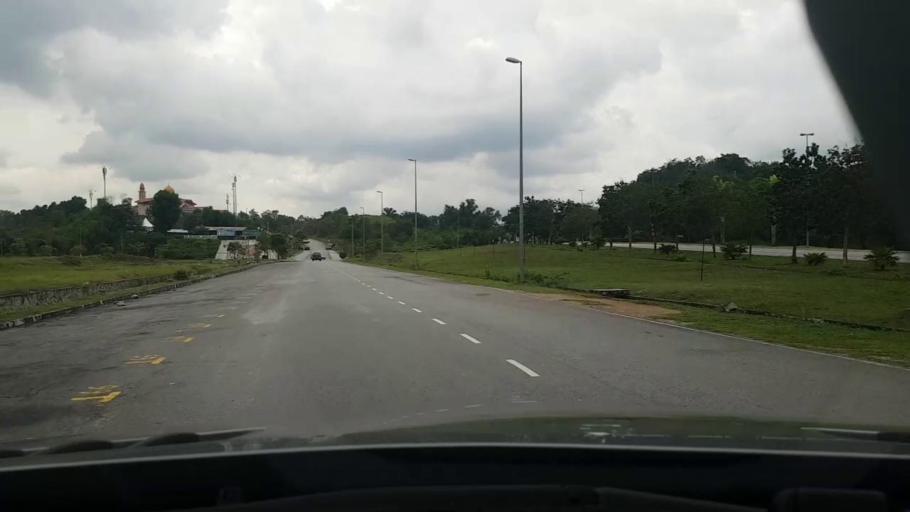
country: MY
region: Selangor
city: Subang Jaya
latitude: 2.9812
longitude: 101.6180
